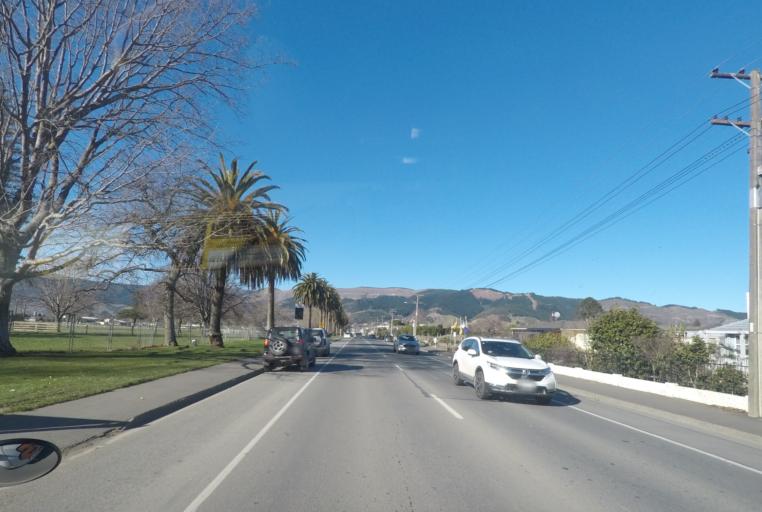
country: NZ
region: Tasman
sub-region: Tasman District
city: Richmond
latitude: -41.3326
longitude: 173.1775
